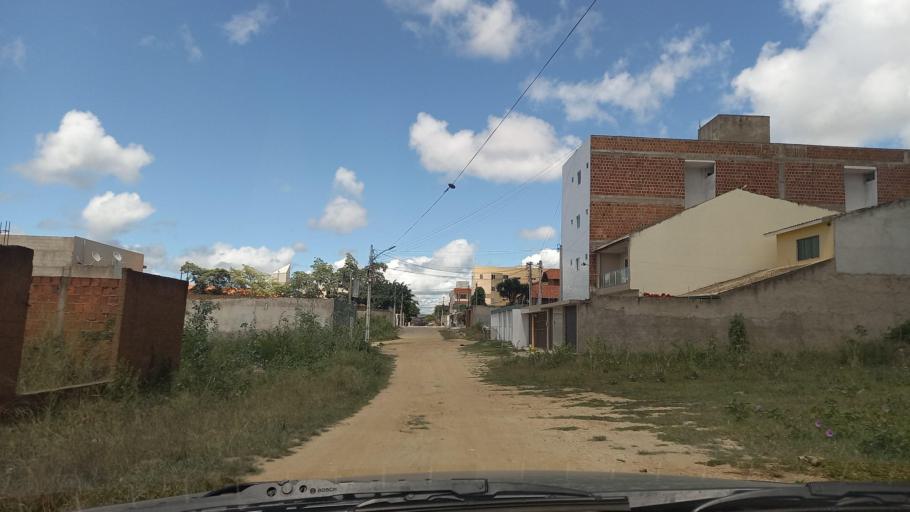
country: BR
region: Pernambuco
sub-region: Caruaru
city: Caruaru
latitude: -8.2659
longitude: -35.9629
